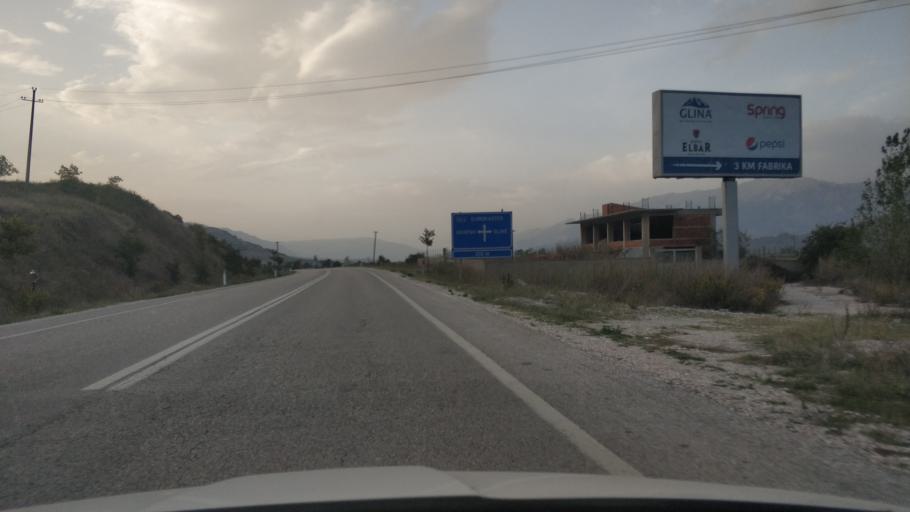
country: AL
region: Gjirokaster
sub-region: Rrethi i Gjirokastres
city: Libohove
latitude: 39.9486
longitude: 20.2579
